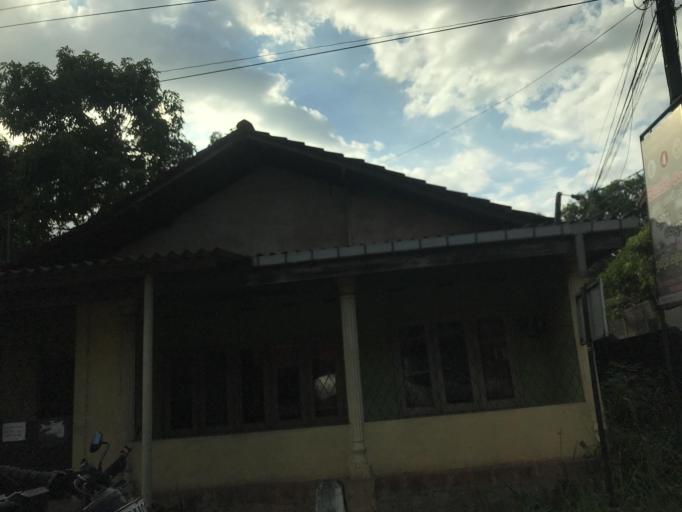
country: LK
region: Western
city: Gampaha
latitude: 7.0807
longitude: 79.9871
